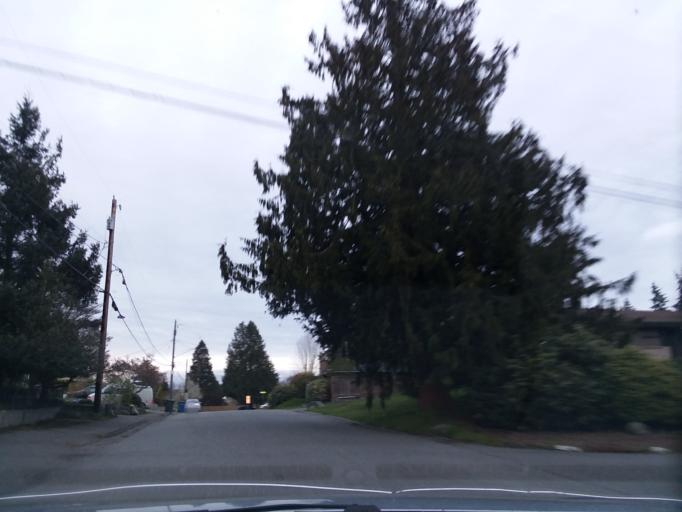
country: US
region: Washington
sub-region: Snohomish County
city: Lynnwood
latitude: 47.8243
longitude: -122.3279
